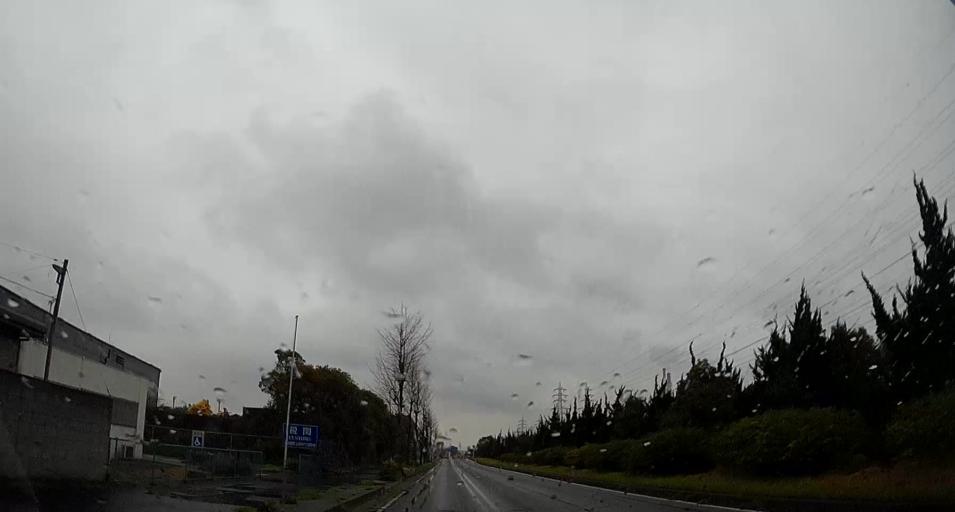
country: JP
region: Chiba
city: Ichihara
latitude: 35.4922
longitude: 140.0445
